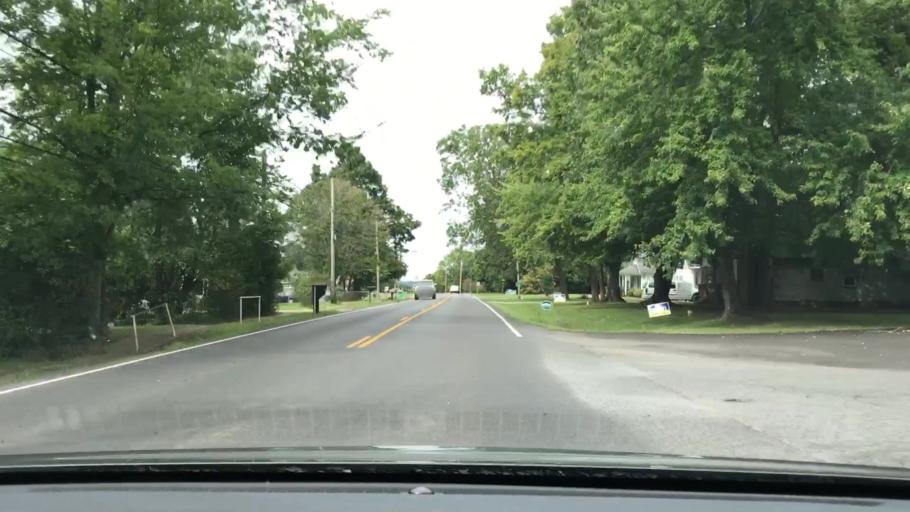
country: US
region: Kentucky
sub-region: Marshall County
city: Benton
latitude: 36.8451
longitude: -88.3498
